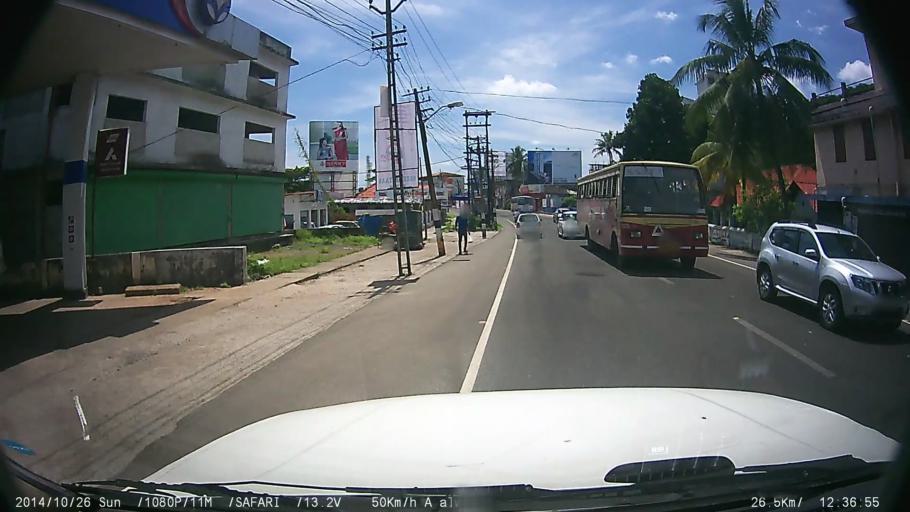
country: IN
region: Kerala
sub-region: Kottayam
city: Kottayam
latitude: 9.5806
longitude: 76.5203
